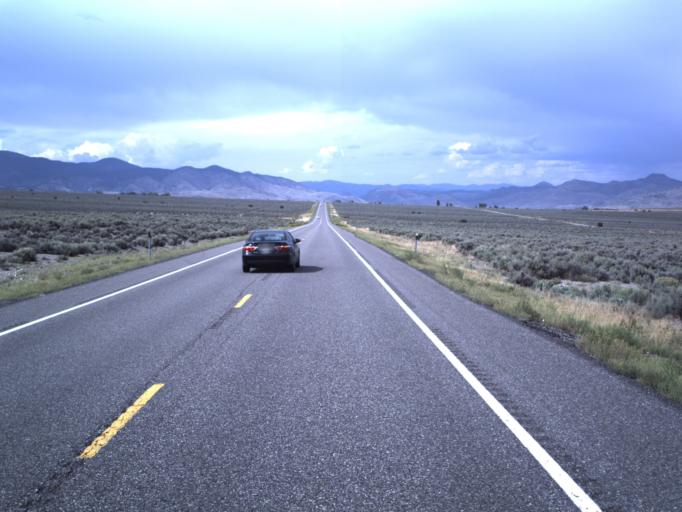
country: US
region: Utah
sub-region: Piute County
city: Junction
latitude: 38.3635
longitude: -112.2235
